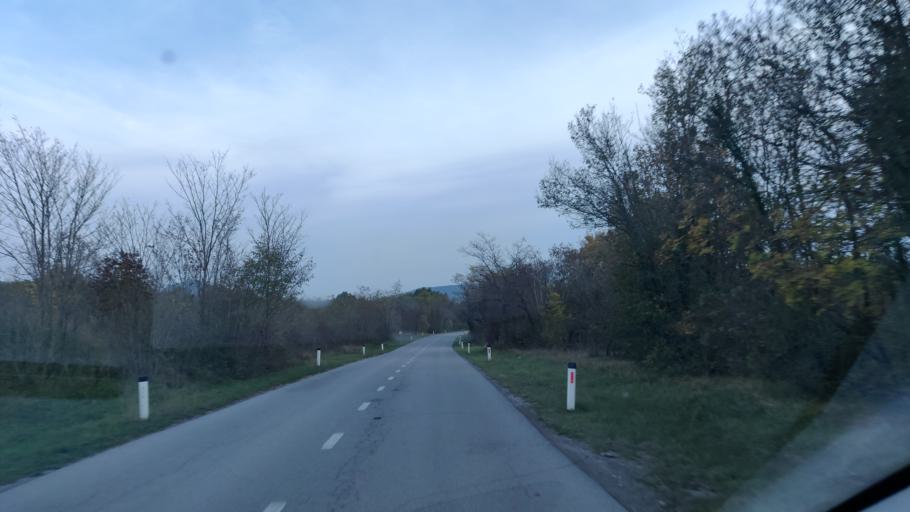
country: SI
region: Sezana
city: Sezana
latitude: 45.7586
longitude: 13.9149
